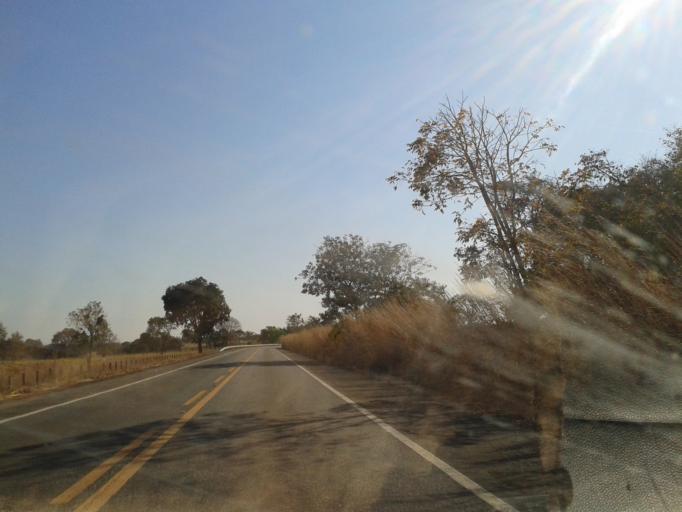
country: BR
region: Goias
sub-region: Mozarlandia
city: Mozarlandia
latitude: -14.8742
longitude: -50.5520
